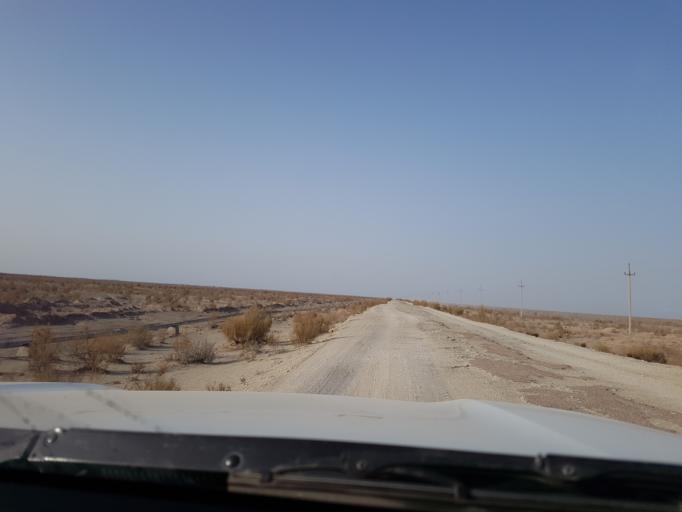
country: UZ
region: Karakalpakstan
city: Shumanay Shahri
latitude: 42.0039
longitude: 58.0717
